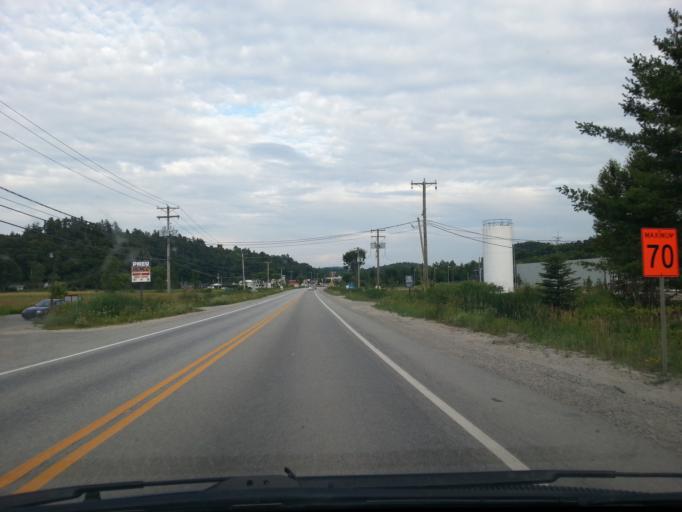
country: CA
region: Quebec
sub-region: Outaouais
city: Wakefield
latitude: 45.6201
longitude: -75.9257
